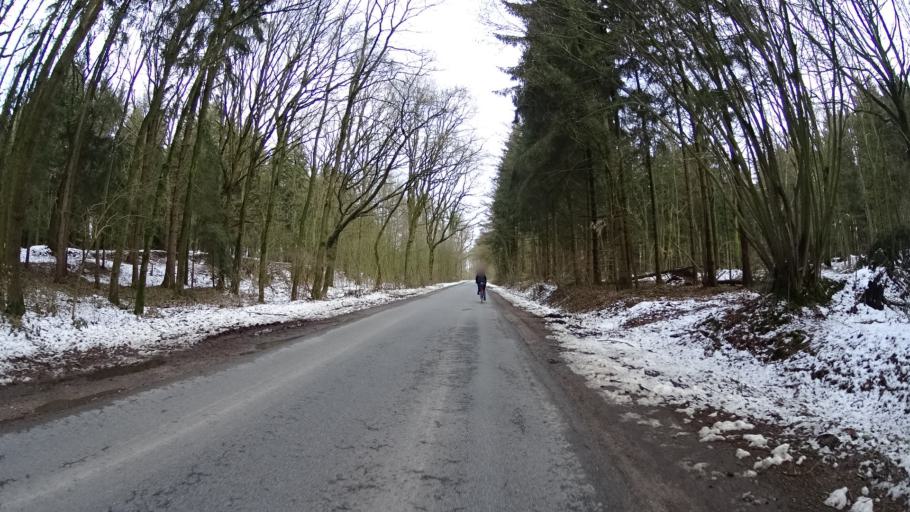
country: DE
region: Schleswig-Holstein
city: Loptin
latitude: 54.1893
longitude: 10.2263
